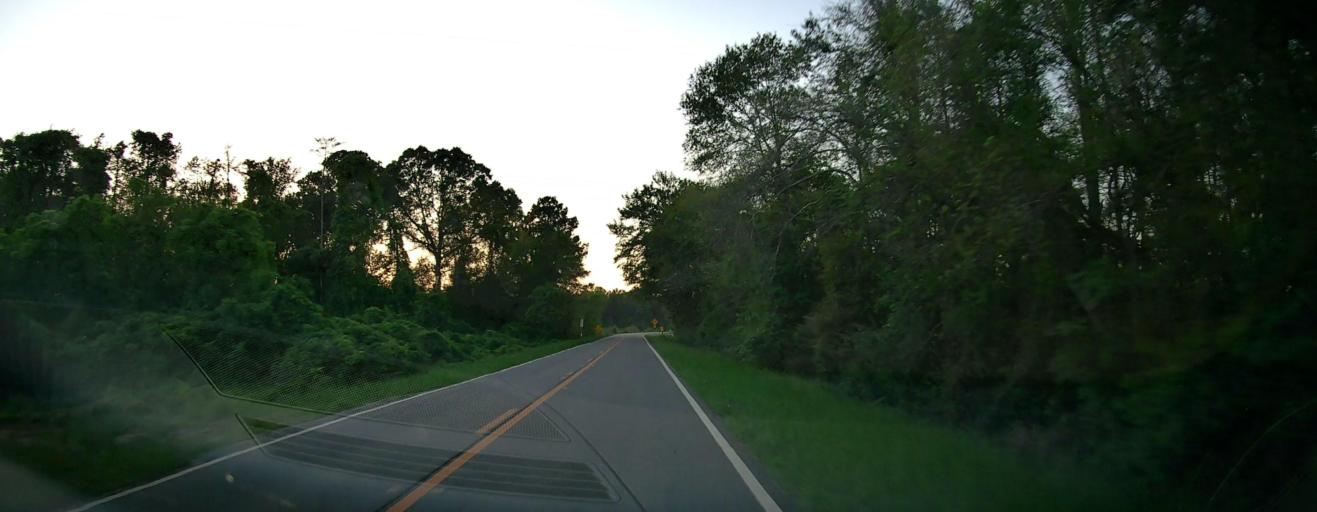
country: US
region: Georgia
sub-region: Wilcox County
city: Rochelle
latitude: 31.7986
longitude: -83.4495
